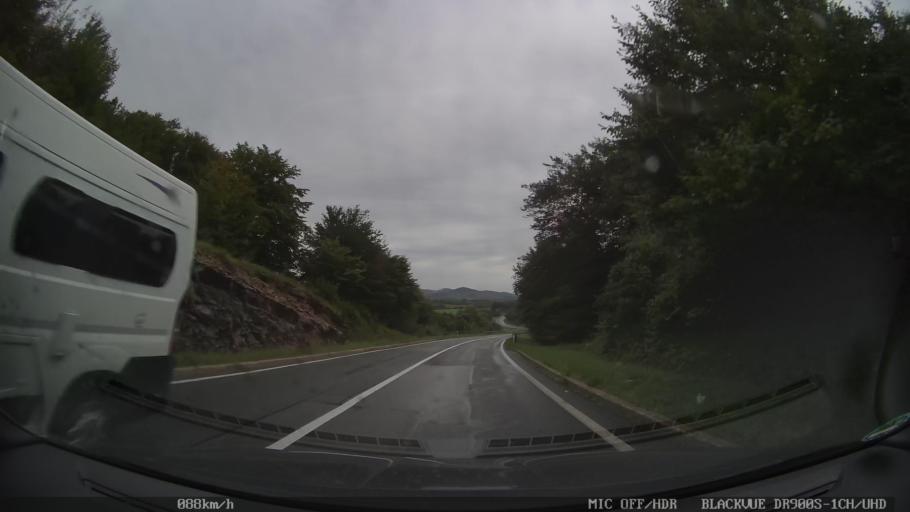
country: HR
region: Licko-Senjska
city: Brinje
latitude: 44.9602
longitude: 15.0920
